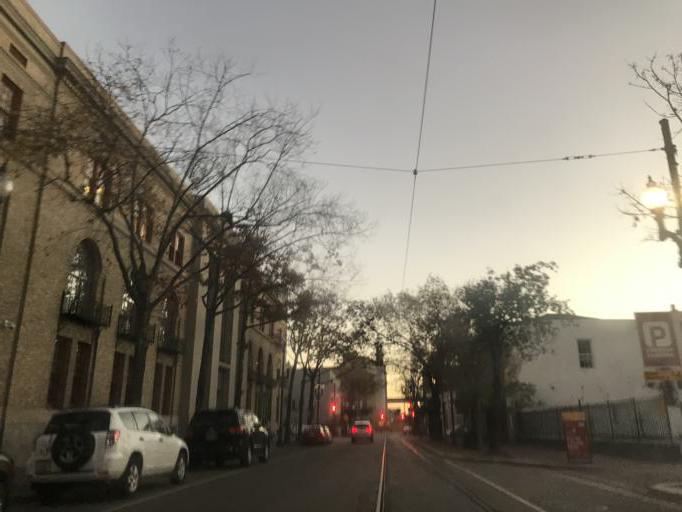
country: US
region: Louisiana
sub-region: Orleans Parish
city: New Orleans
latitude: 29.9451
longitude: -90.0720
